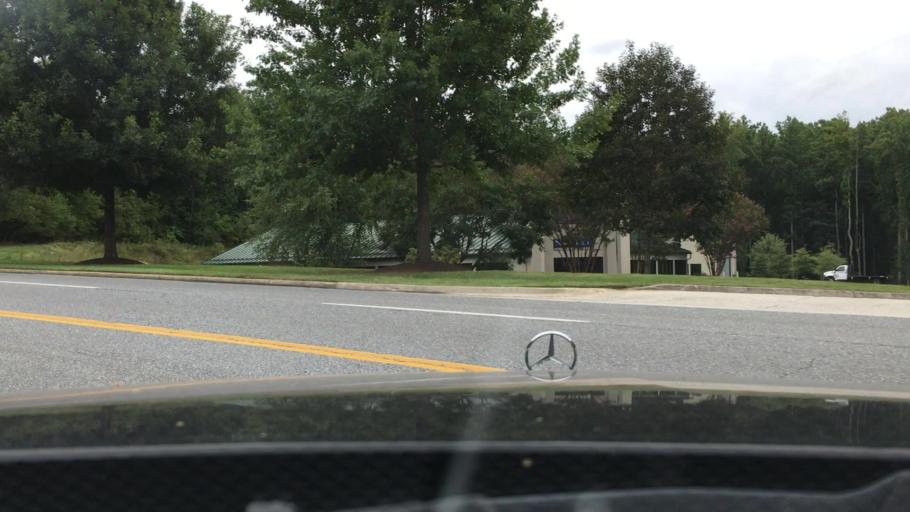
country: US
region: Virginia
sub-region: City of Lynchburg
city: West Lynchburg
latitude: 37.3998
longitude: -79.2335
